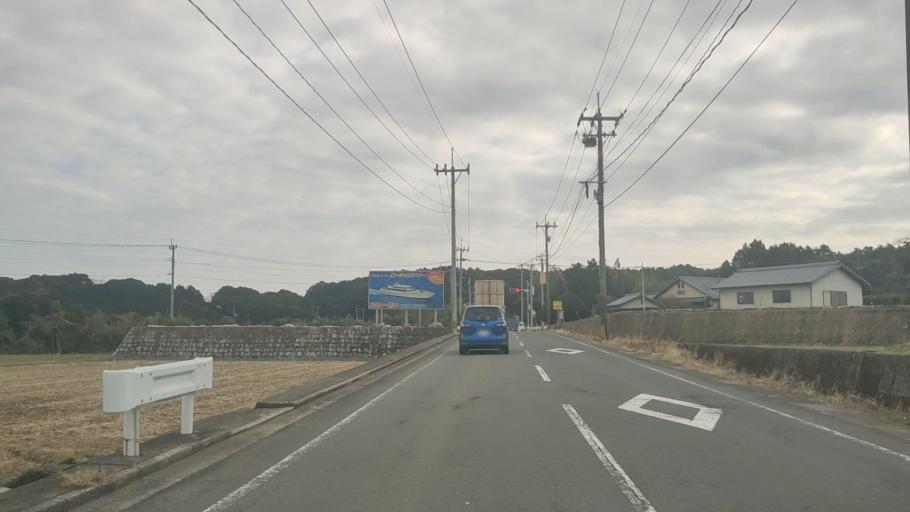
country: JP
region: Nagasaki
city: Shimabara
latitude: 32.8530
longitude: 130.2550
